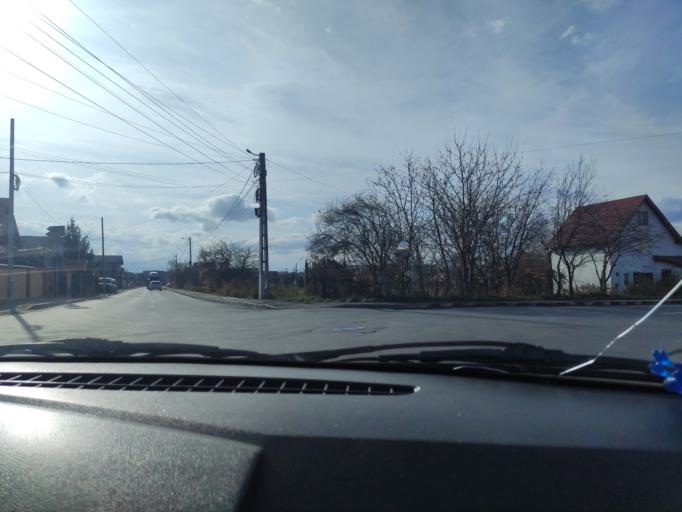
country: RO
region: Brasov
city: Codlea
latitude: 45.7044
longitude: 25.4567
